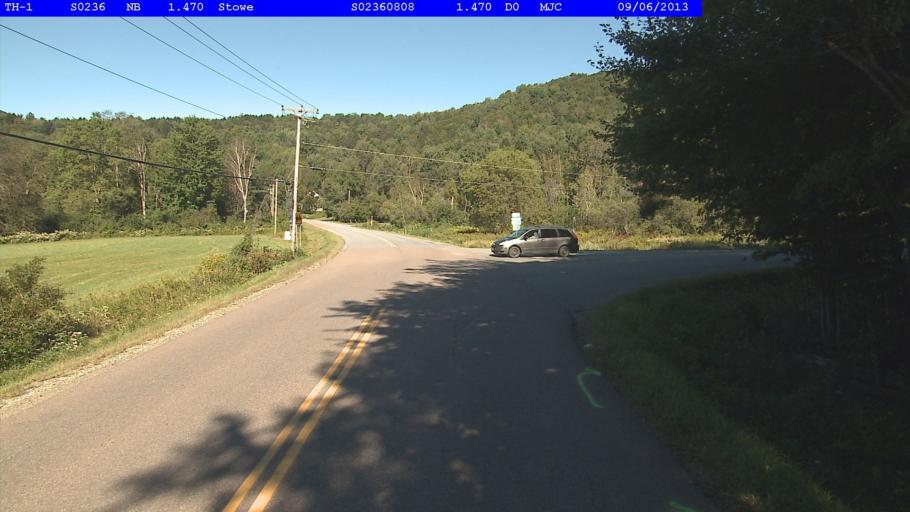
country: US
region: Vermont
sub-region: Washington County
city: Waterbury
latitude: 44.4474
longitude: -72.7330
